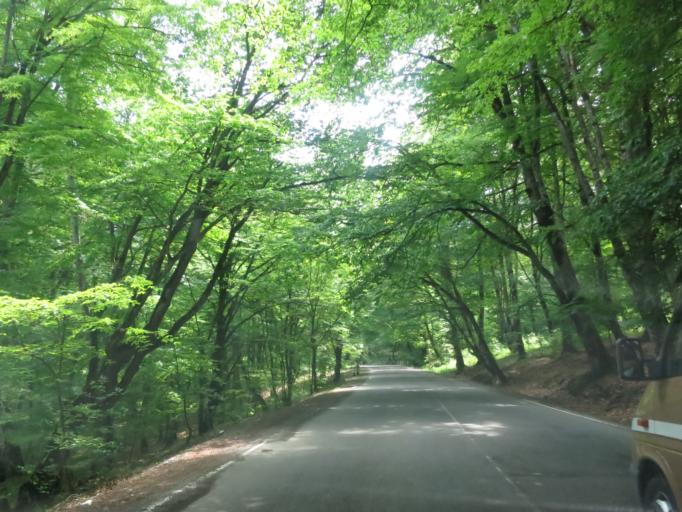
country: GE
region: Kakheti
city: Sagarejo
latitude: 41.8631
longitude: 45.3363
